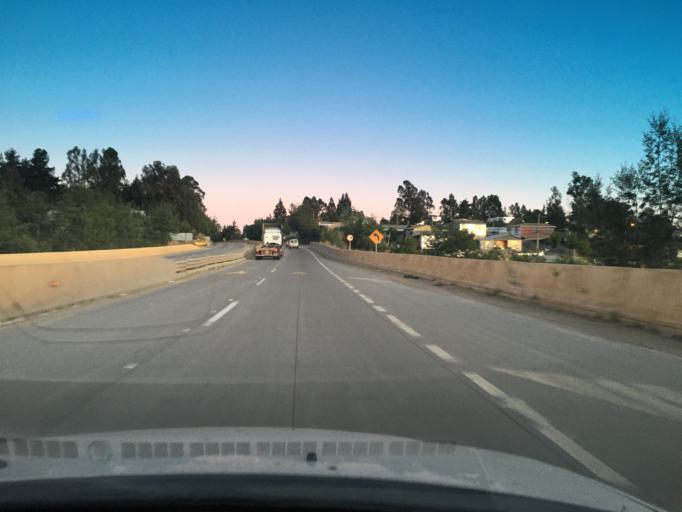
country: CL
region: Valparaiso
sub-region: Provincia de Valparaiso
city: Vina del Mar
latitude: -33.1067
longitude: -71.5715
